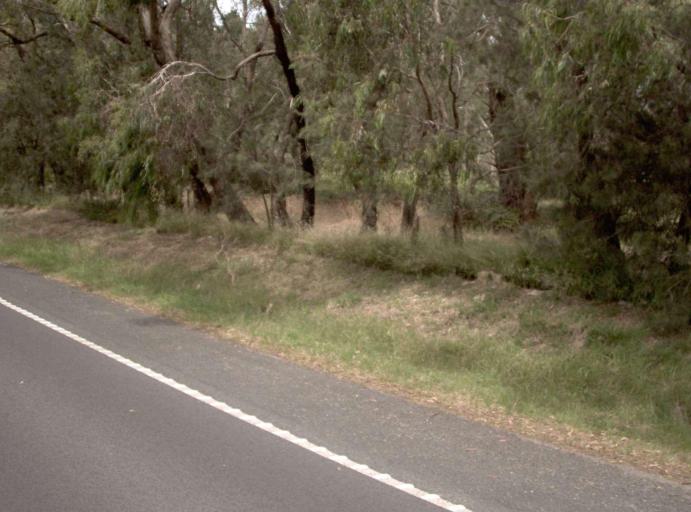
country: AU
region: Victoria
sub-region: Mornington Peninsula
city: Tyabb
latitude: -38.2463
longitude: 145.2150
